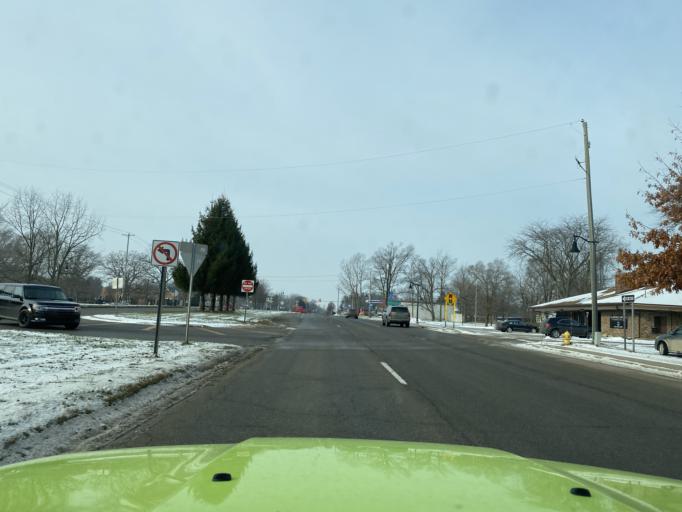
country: US
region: Michigan
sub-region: Ottawa County
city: Allendale
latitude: 42.9725
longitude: -85.9512
